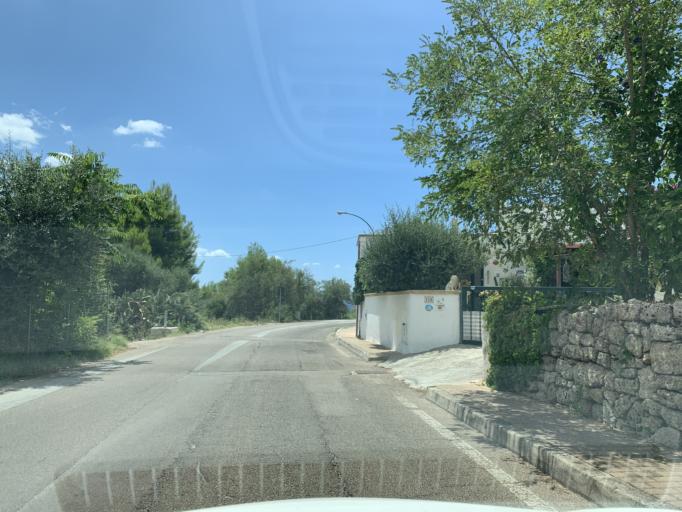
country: IT
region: Apulia
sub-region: Provincia di Lecce
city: Santa Cesarea Terme
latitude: 40.0339
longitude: 18.4520
